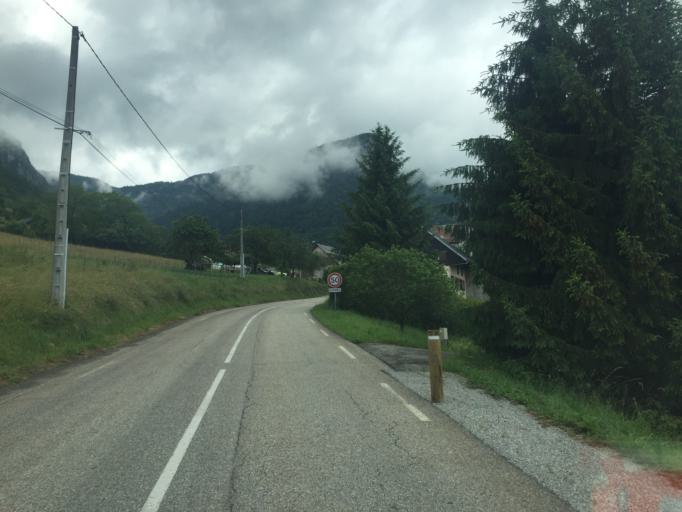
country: FR
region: Rhone-Alpes
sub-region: Departement de la Savoie
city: Barby
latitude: 45.5841
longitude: 6.0335
